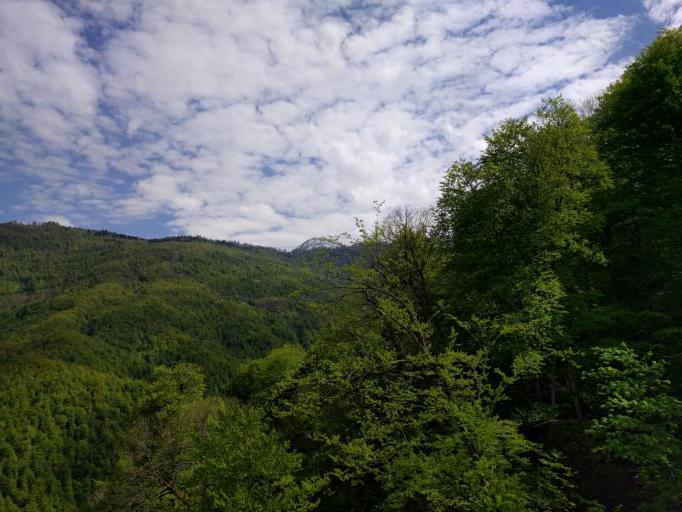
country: RU
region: Krasnodarskiy
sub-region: Sochi City
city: Krasnaya Polyana
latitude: 43.6670
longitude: 40.3056
